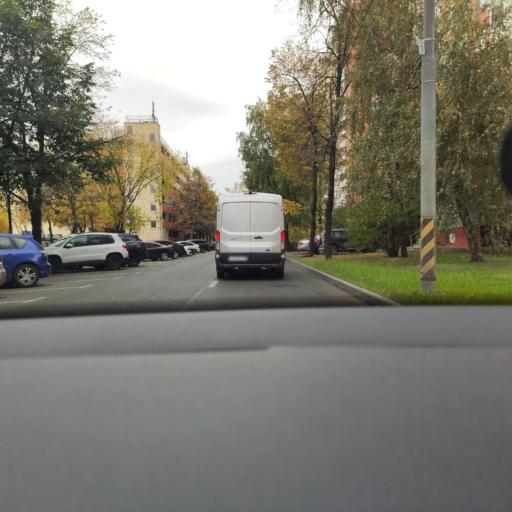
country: RU
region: Moscow
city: Kozeyevo
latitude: 55.8900
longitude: 37.6462
